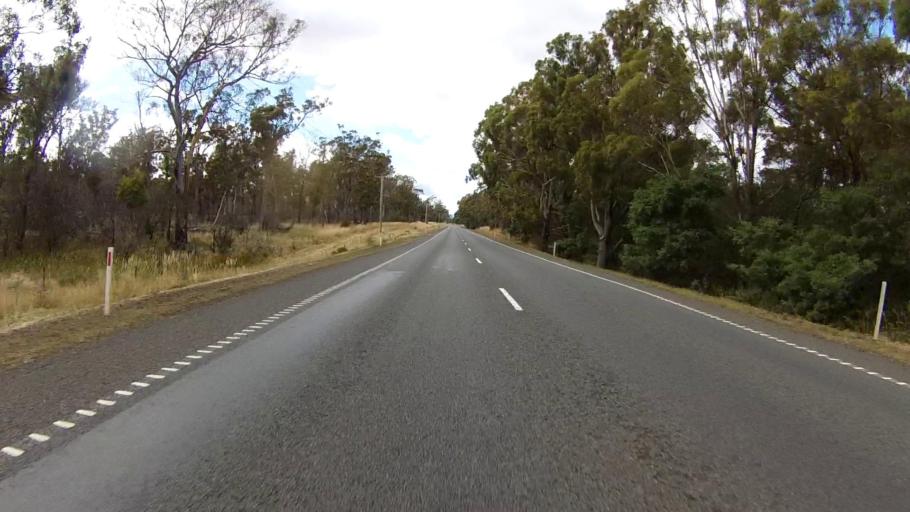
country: AU
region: Tasmania
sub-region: Northern Midlands
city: Evandale
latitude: -41.8228
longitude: 147.4271
